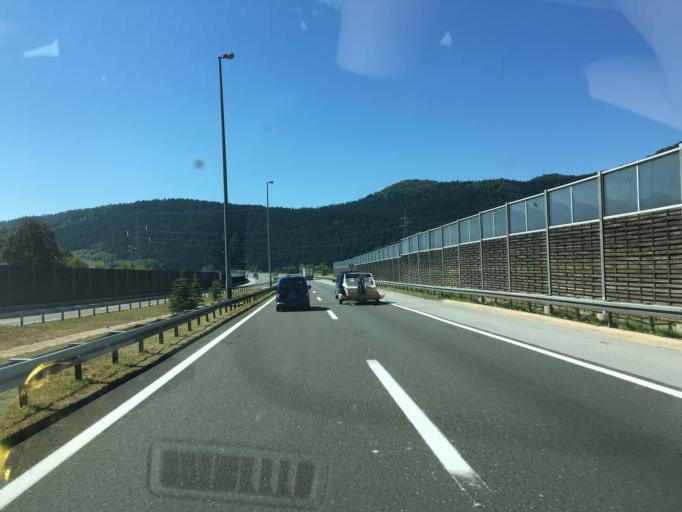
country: HR
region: Licko-Senjska
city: Otocac
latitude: 44.8701
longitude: 15.2073
